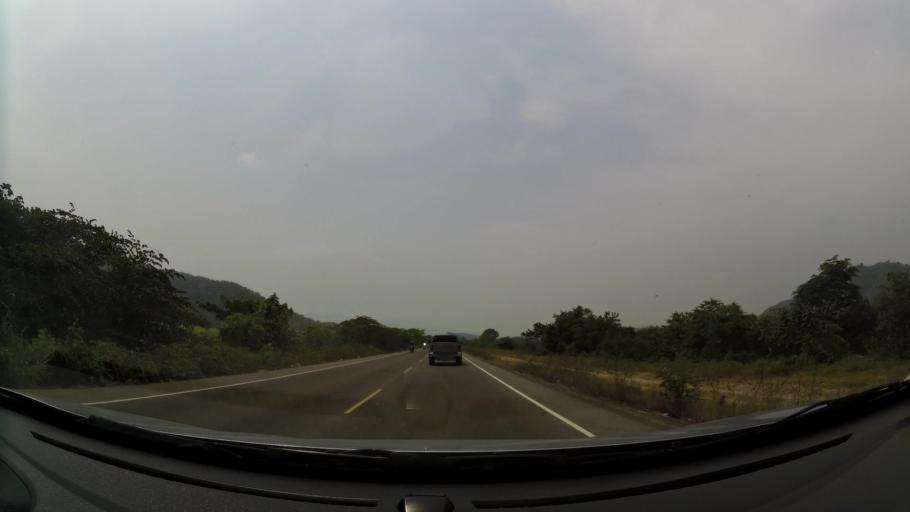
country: HN
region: Cortes
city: Potrerillos
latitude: 15.2539
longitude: -87.9569
